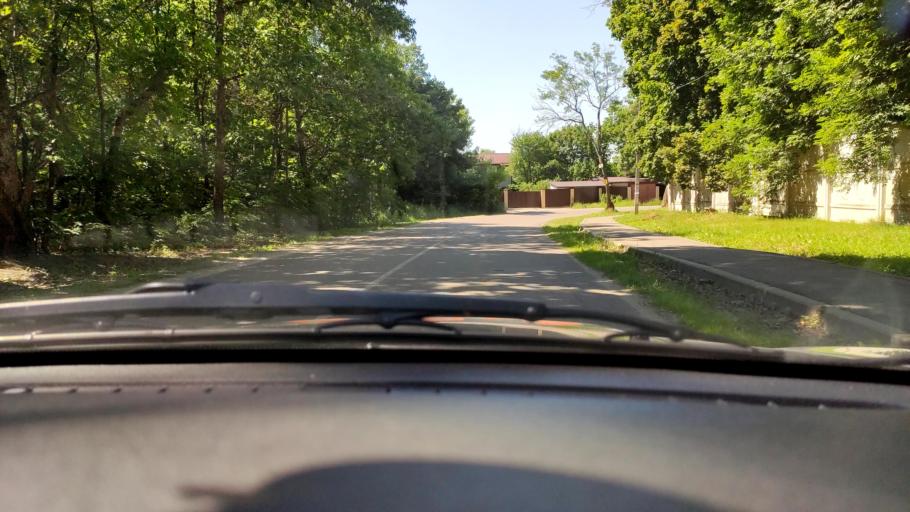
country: RU
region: Voronezj
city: Ramon'
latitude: 51.8236
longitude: 39.2616
